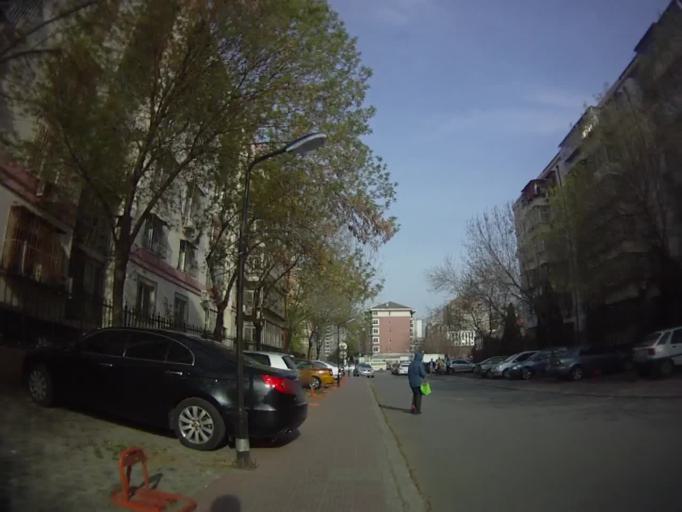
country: CN
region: Beijing
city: Longtan
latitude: 39.8981
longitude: 116.4433
